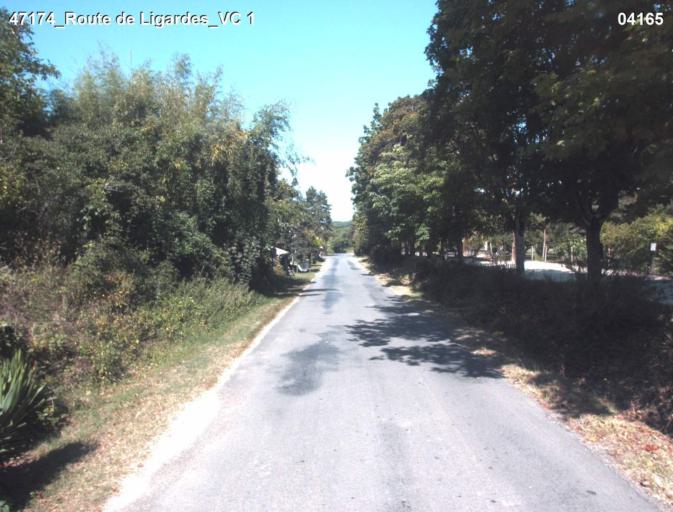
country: FR
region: Midi-Pyrenees
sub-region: Departement du Gers
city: Condom
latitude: 44.0343
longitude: 0.3730
